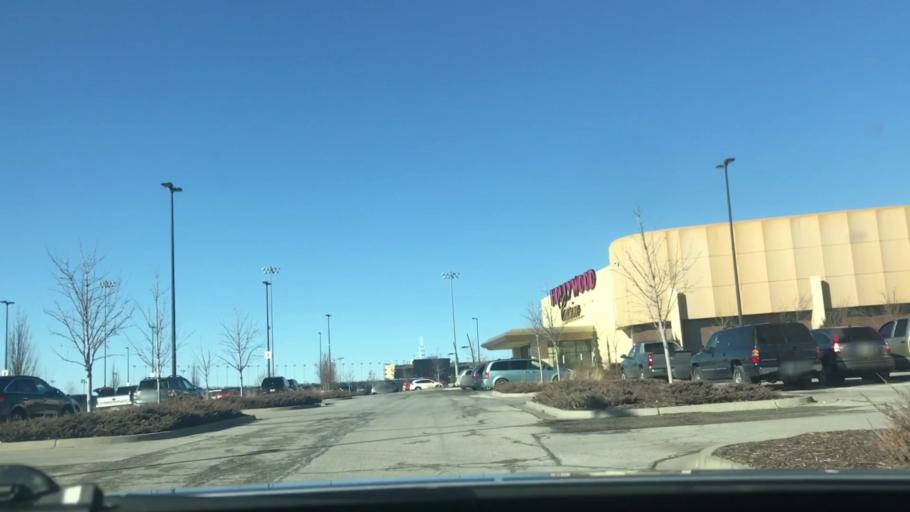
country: US
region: Kansas
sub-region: Wyandotte County
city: Edwardsville
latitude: 39.1105
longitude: -94.8277
